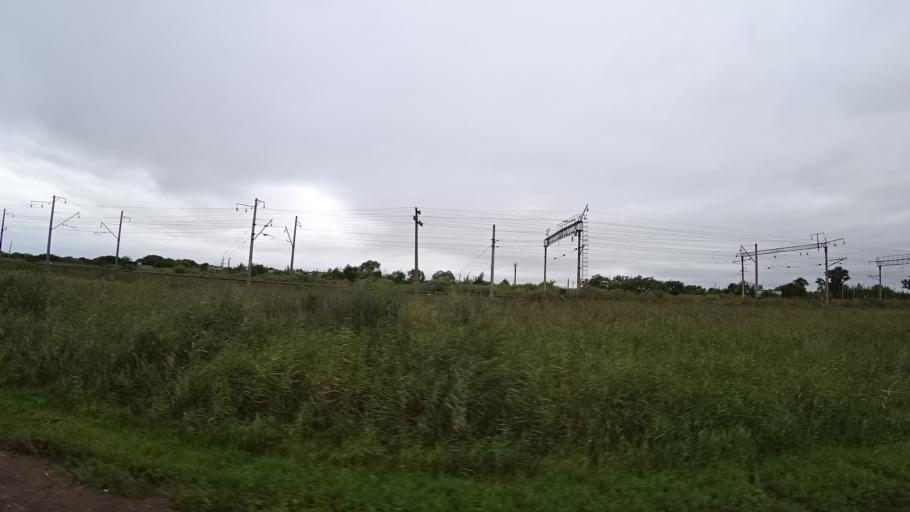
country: RU
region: Primorskiy
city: Chernigovka
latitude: 44.3340
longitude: 132.5254
